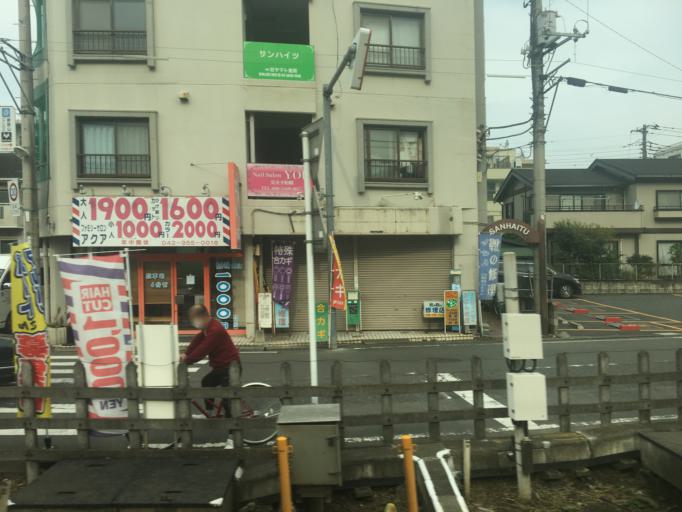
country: JP
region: Saitama
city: Sayama
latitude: 35.8732
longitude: 139.4324
